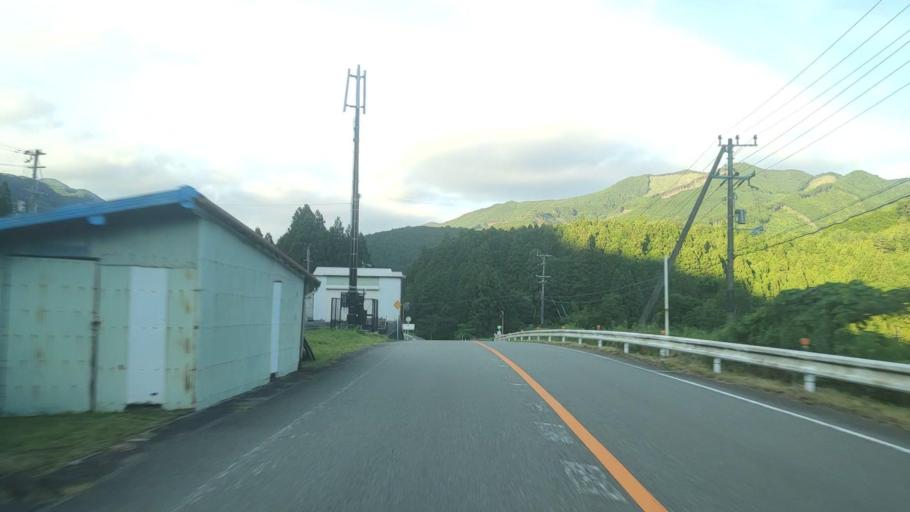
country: JP
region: Wakayama
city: Tanabe
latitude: 33.8194
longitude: 135.6245
